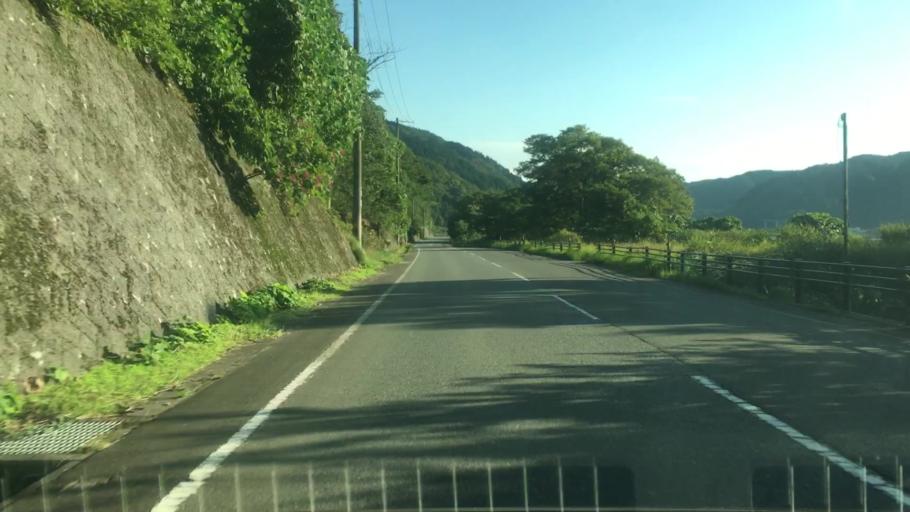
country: JP
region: Hyogo
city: Toyooka
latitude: 35.6024
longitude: 134.8059
